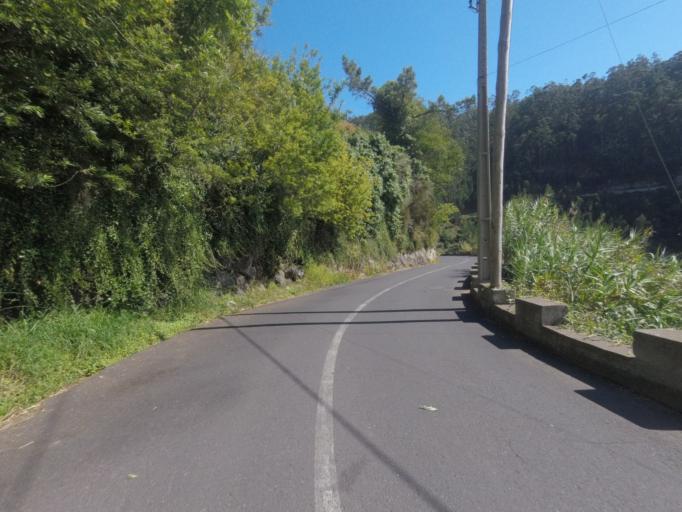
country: PT
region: Madeira
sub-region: Ribeira Brava
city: Campanario
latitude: 32.6899
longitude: -17.0311
